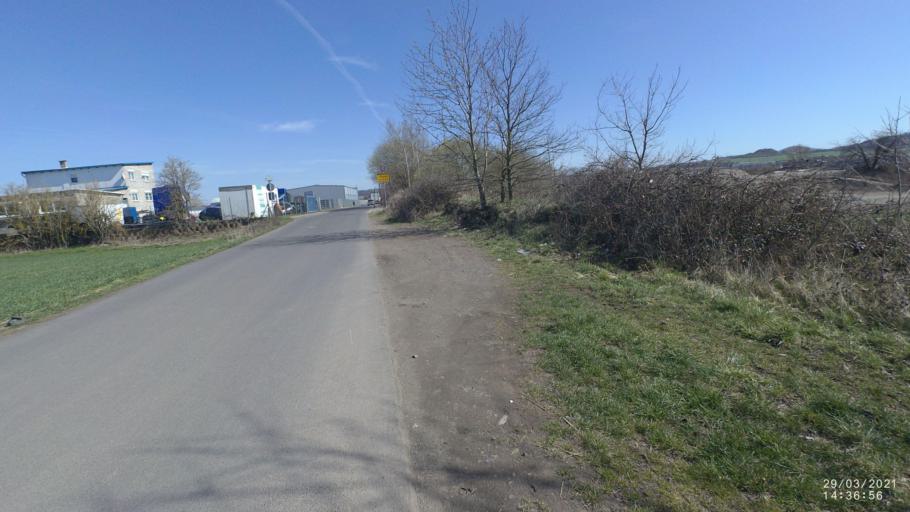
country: DE
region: Rheinland-Pfalz
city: Kretz
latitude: 50.3911
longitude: 7.3769
